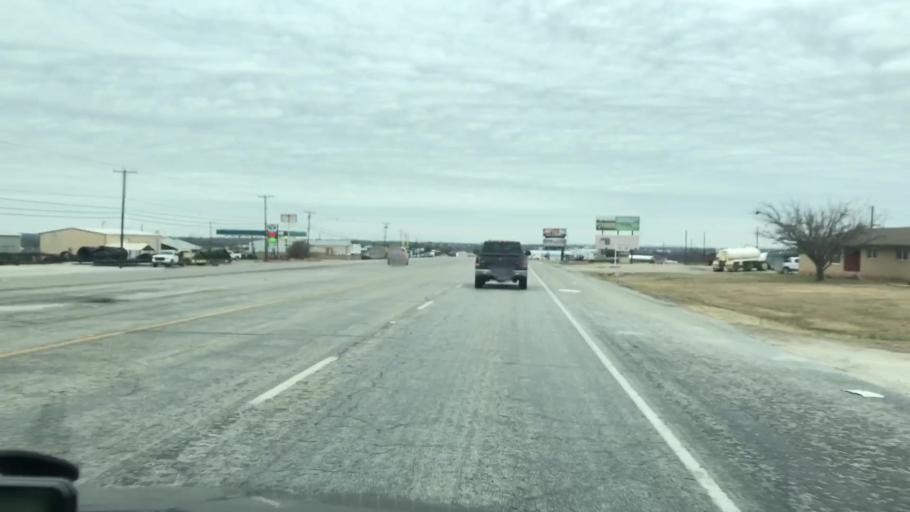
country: US
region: Texas
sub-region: Jack County
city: Jacksboro
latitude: 33.1977
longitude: -98.1468
